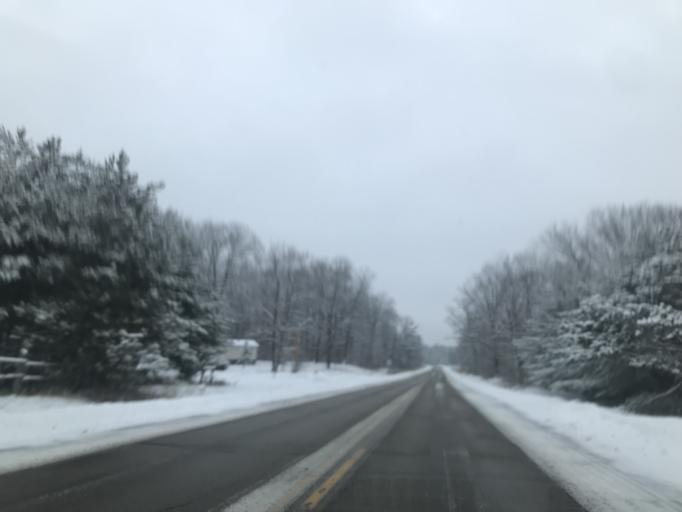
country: US
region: Wisconsin
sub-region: Oconto County
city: Oconto Falls
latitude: 44.8630
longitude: -88.1187
